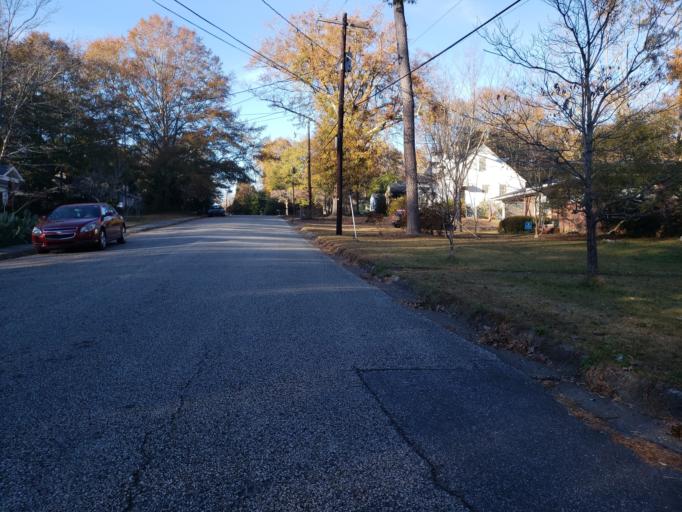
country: US
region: Alabama
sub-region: Lee County
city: Auburn
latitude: 32.5941
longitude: -85.4738
